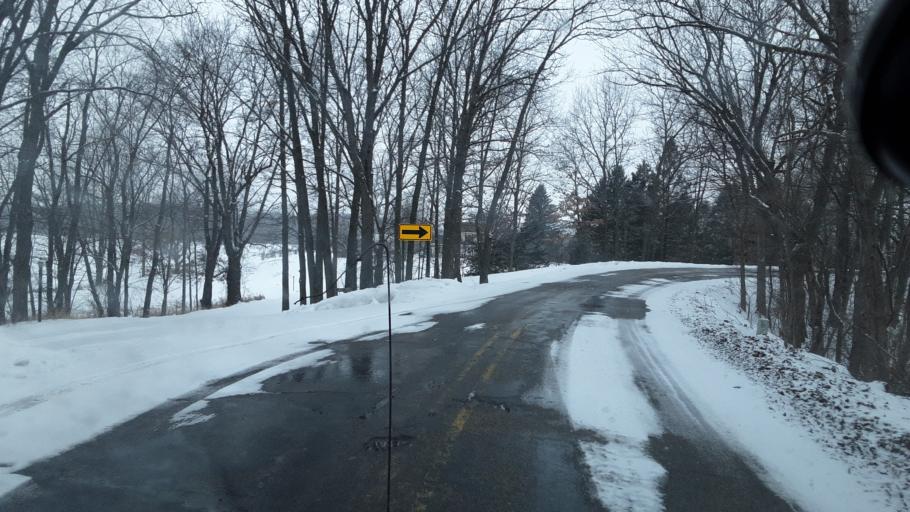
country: US
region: Michigan
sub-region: Ingham County
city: Leslie
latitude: 42.4878
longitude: -84.3643
